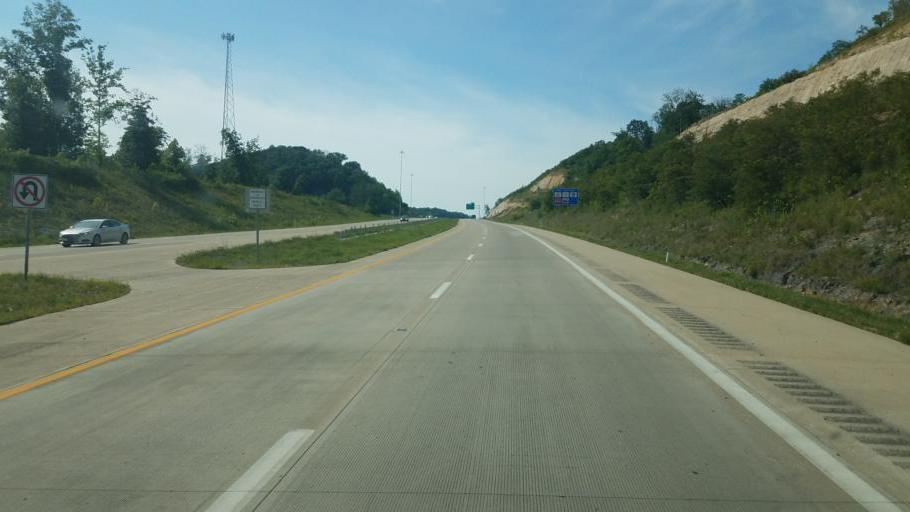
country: US
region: Ohio
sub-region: Athens County
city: Nelsonville
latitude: 39.4347
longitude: -82.1991
